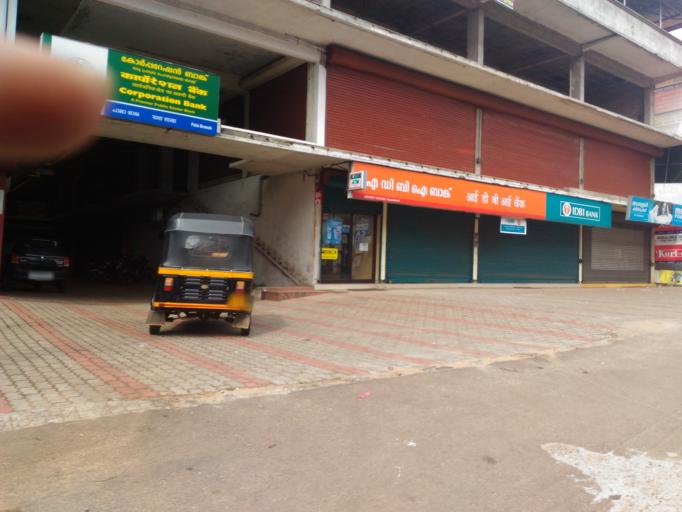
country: IN
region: Kerala
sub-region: Kottayam
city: Lalam
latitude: 9.7096
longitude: 76.6768
